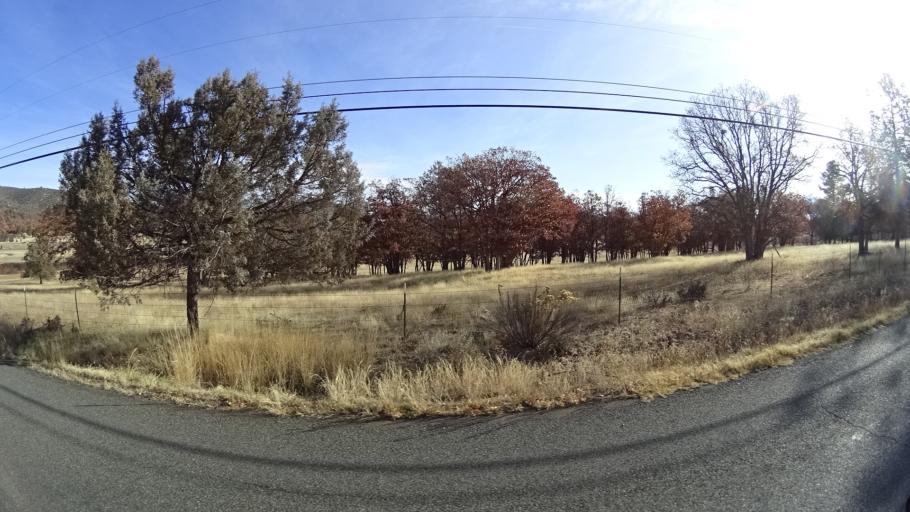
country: US
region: California
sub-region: Siskiyou County
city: Yreka
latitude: 41.6700
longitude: -122.6232
